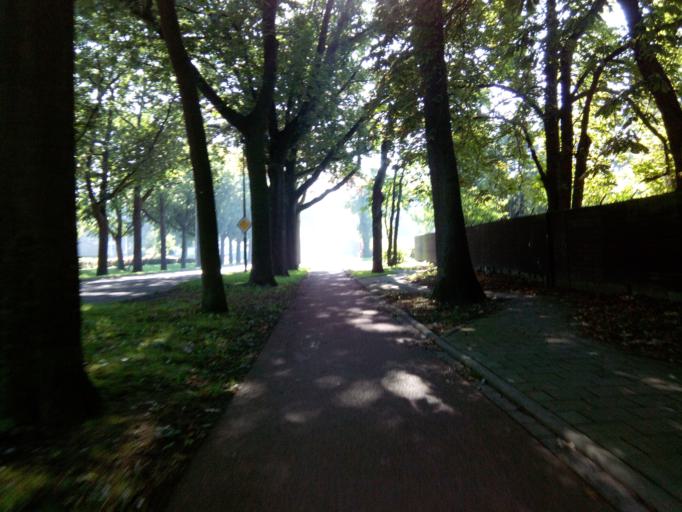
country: NL
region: Utrecht
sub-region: Gemeente Utrechtse Heuvelrug
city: Amerongen
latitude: 51.9999
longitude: 5.4644
